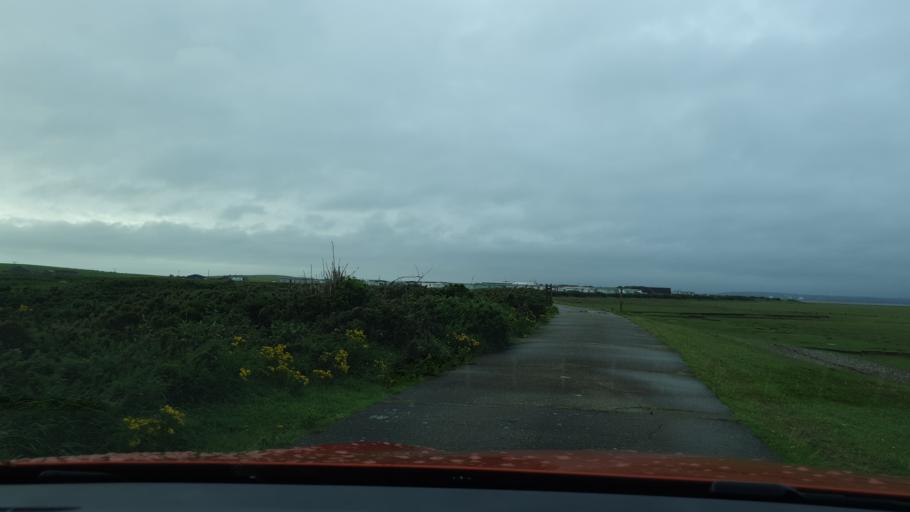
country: GB
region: England
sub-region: Cumbria
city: Barrow in Furness
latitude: 54.0535
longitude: -3.2070
